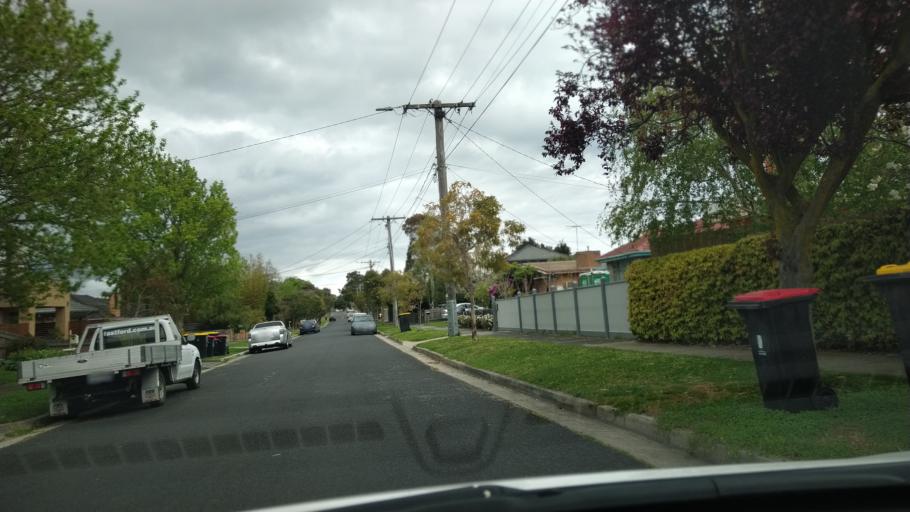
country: AU
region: Victoria
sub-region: Kingston
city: Mentone
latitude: -37.9627
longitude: 145.0692
